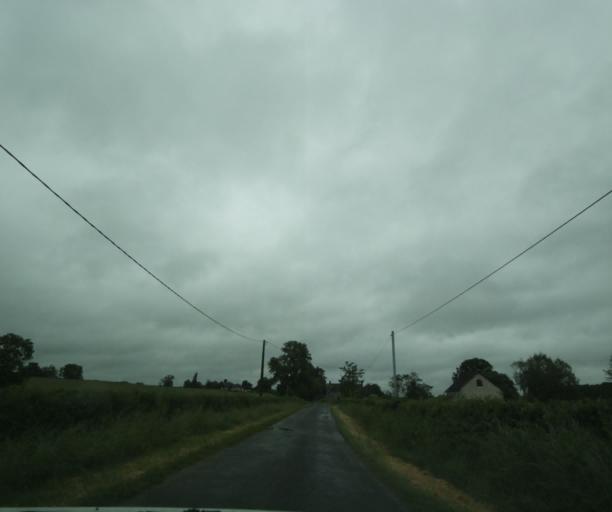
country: FR
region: Bourgogne
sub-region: Departement de Saone-et-Loire
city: Palinges
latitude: 46.5721
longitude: 4.2153
